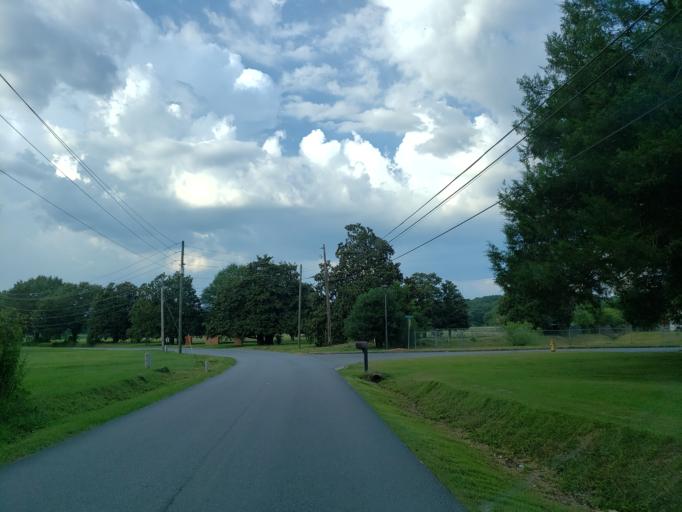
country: US
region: Georgia
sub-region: Polk County
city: Rockmart
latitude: 34.0022
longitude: -85.0294
